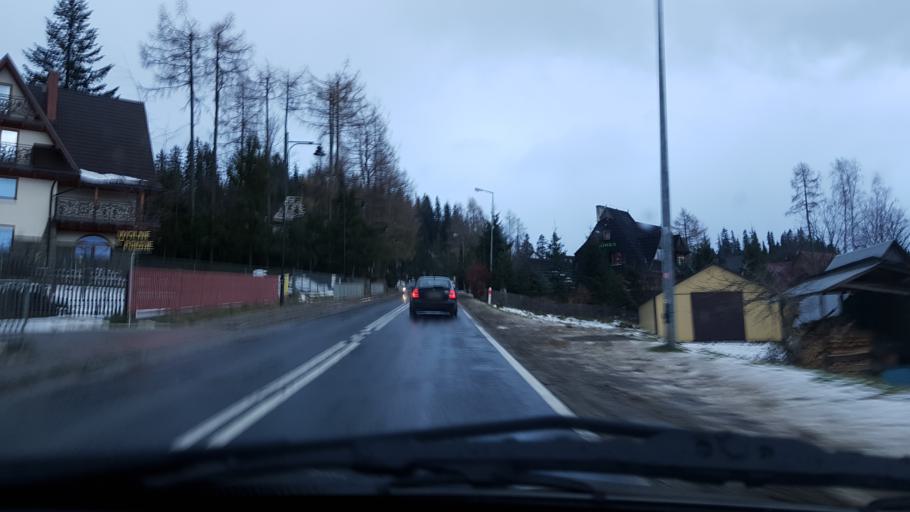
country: PL
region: Lesser Poland Voivodeship
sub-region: Powiat tatrzanski
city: Bukowina Tatrzanska
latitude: 49.3254
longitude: 20.1021
